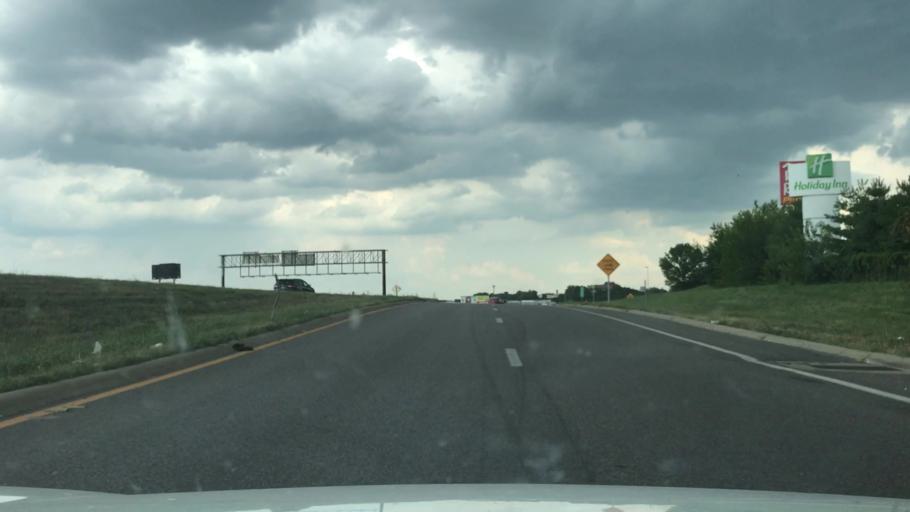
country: US
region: Missouri
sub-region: Saint Louis County
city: Richmond Heights
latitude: 38.6184
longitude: -90.2867
